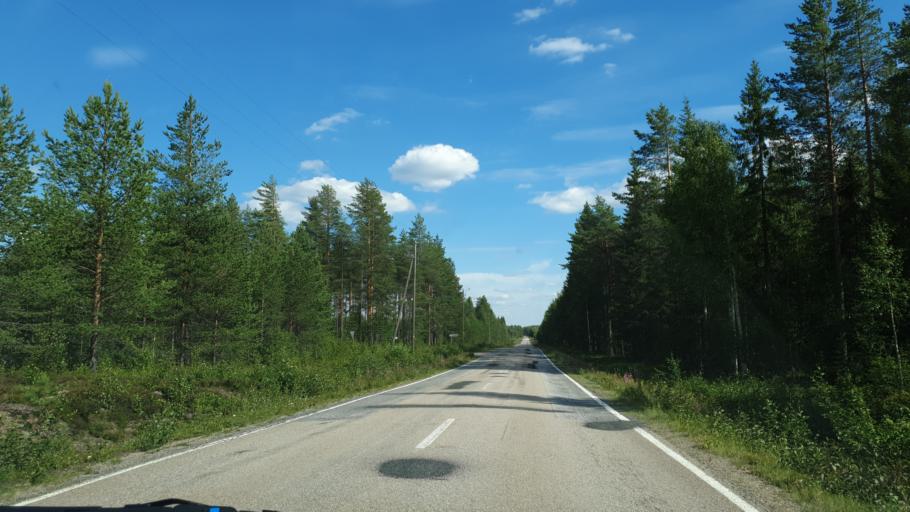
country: FI
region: Kainuu
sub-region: Kehys-Kainuu
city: Kuhmo
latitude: 64.2115
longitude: 29.0182
